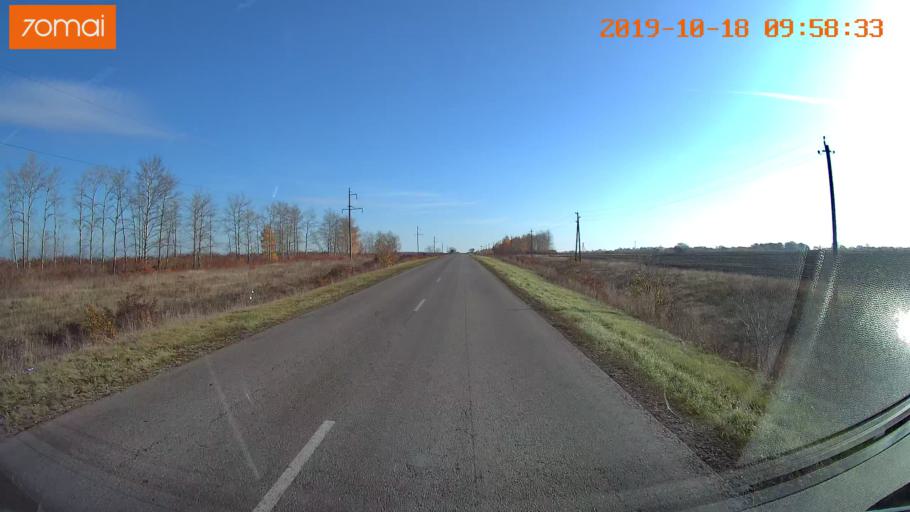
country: RU
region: Tula
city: Kurkino
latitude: 53.3753
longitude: 38.4430
